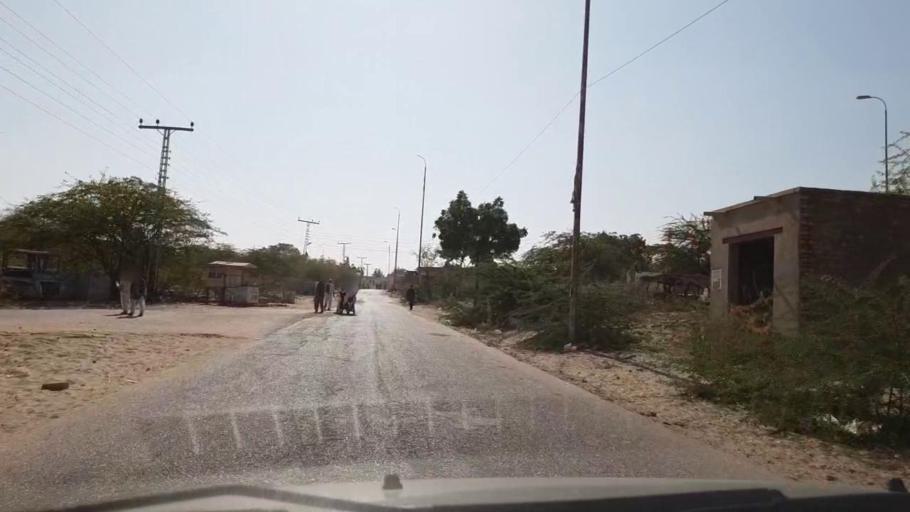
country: PK
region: Sindh
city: Diplo
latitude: 24.4728
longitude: 69.5800
